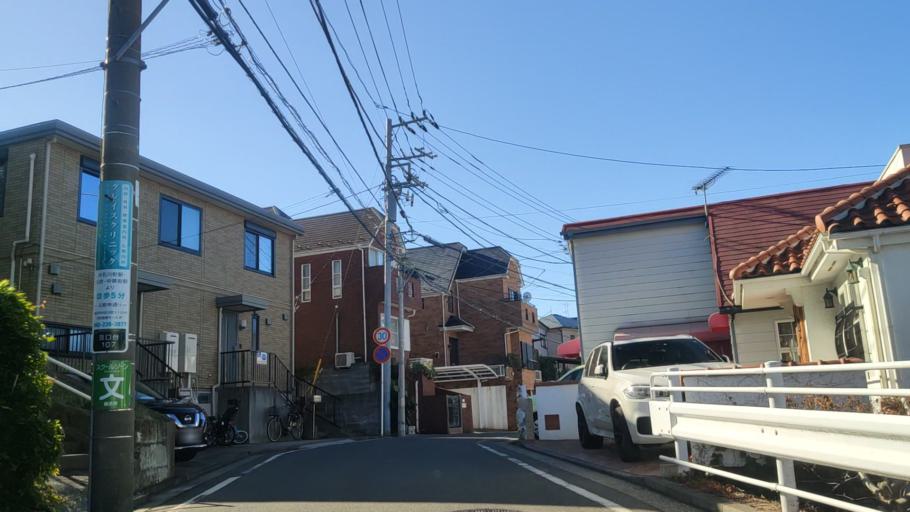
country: JP
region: Kanagawa
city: Yokohama
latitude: 35.4237
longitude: 139.6445
